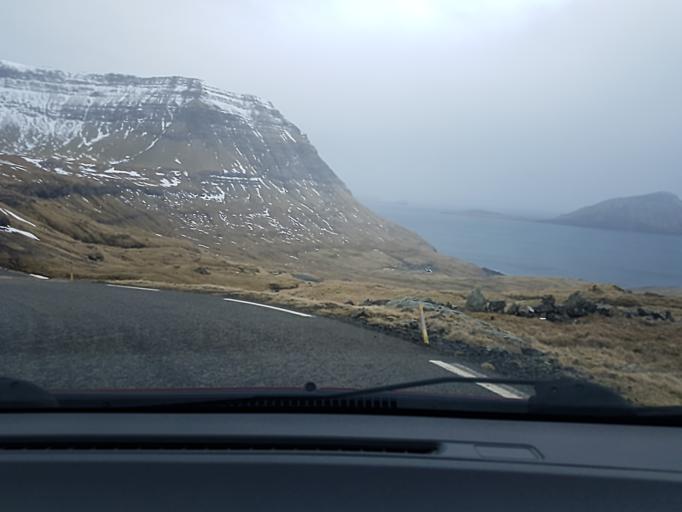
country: FO
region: Streymoy
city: Kollafjordhur
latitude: 62.0504
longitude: -6.9229
